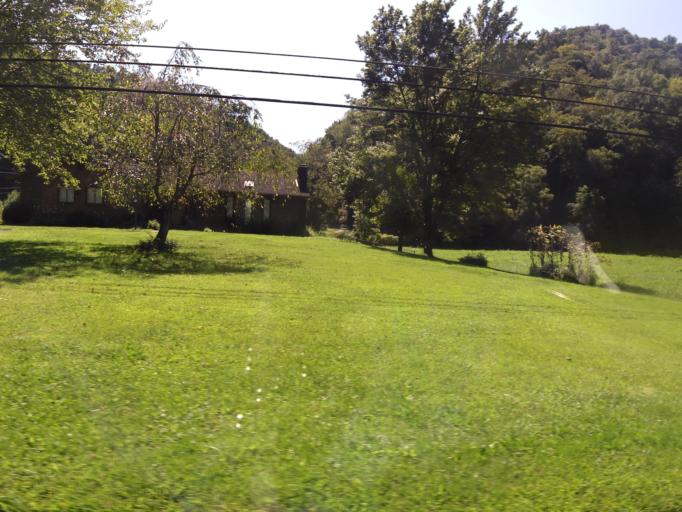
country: US
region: Kentucky
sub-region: Clay County
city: Manchester
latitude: 37.1265
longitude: -83.6317
